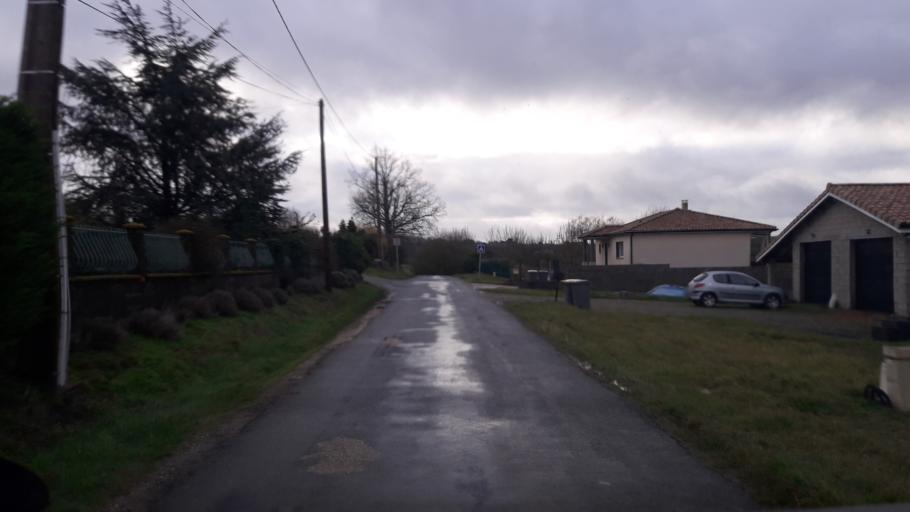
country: FR
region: Midi-Pyrenees
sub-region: Departement de la Haute-Garonne
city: Marquefave
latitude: 43.3058
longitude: 1.2444
